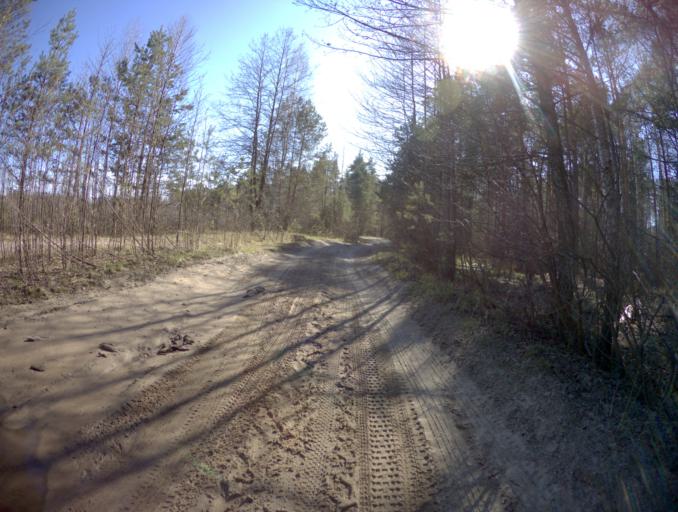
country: RU
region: Vladimir
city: Ivanishchi
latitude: 55.7636
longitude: 40.4079
